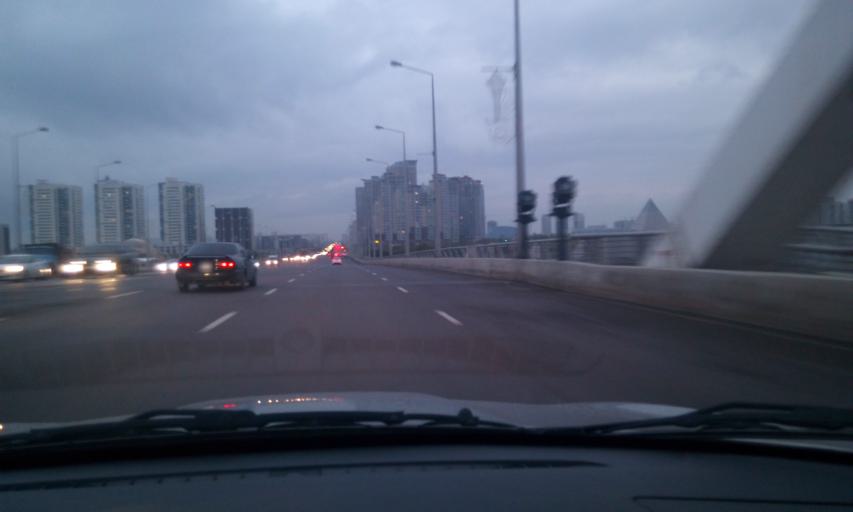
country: KZ
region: Astana Qalasy
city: Astana
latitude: 51.1310
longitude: 71.4479
